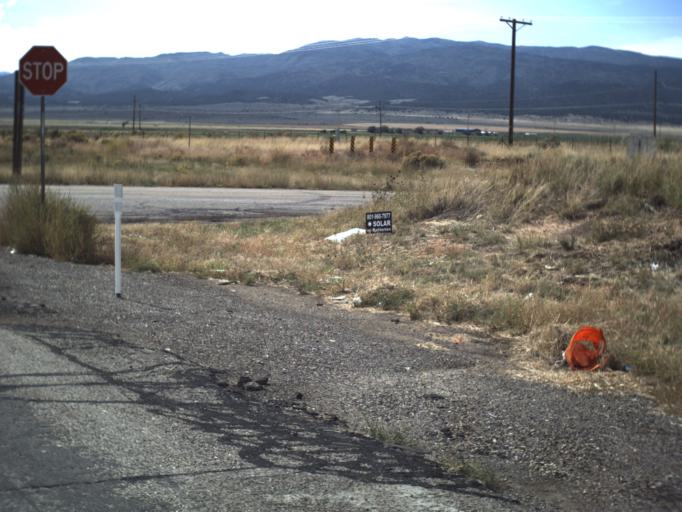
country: US
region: Utah
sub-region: Iron County
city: Cedar City
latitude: 37.6033
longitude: -113.1617
